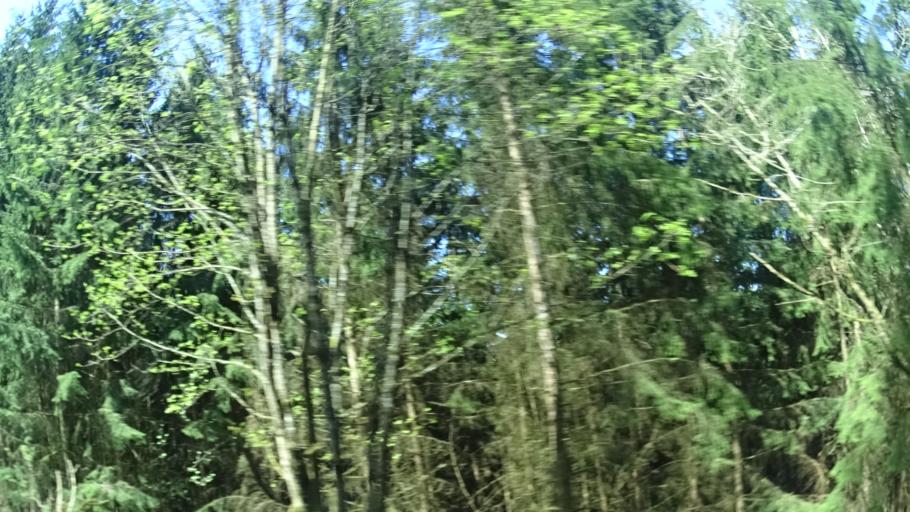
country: DE
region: Thuringia
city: Schleusingen
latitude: 50.4592
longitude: 10.7793
